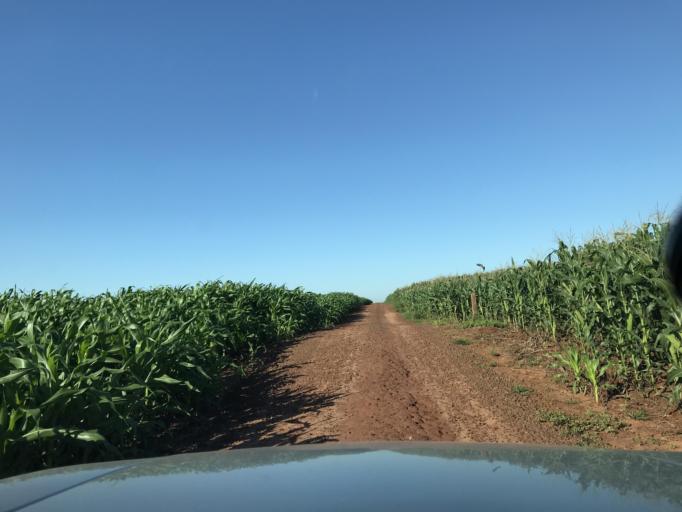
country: BR
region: Parana
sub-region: Palotina
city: Palotina
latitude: -24.2305
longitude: -53.7626
